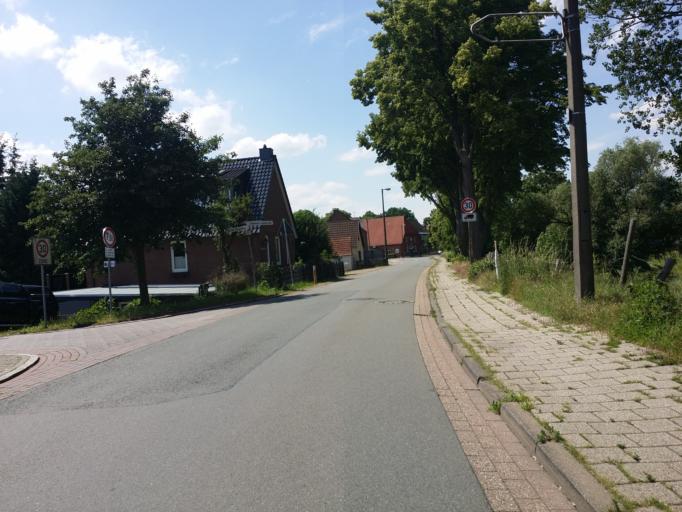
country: DE
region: Lower Saxony
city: Ritterhude
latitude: 53.1106
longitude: 8.7119
